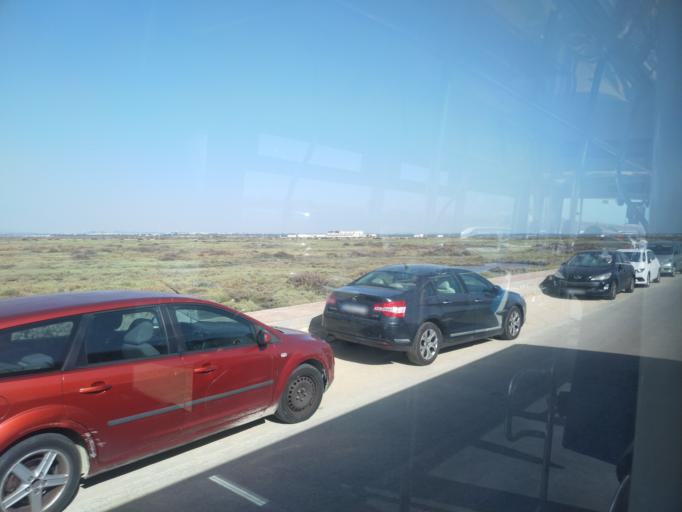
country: ES
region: Andalusia
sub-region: Provincia de Cadiz
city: San Fernando
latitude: 36.4241
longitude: -6.2269
